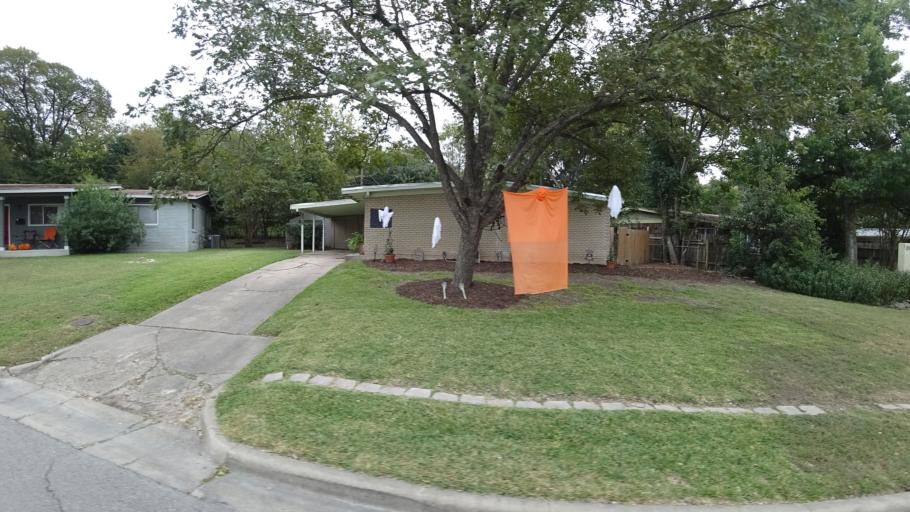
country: US
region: Texas
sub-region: Travis County
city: Austin
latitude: 30.2914
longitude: -97.7598
